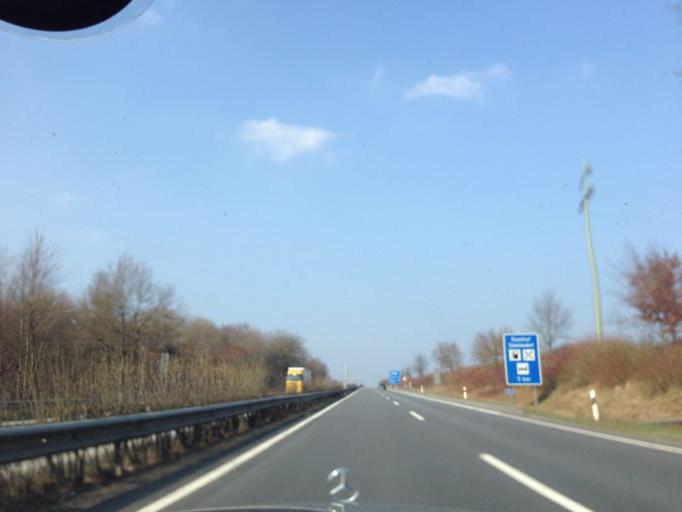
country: DE
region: Schleswig-Holstein
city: Hogersdorf
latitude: 53.9147
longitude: 10.2744
